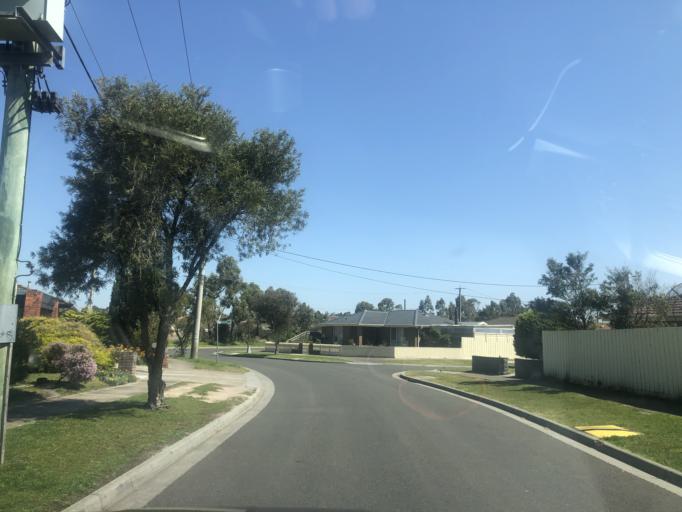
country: AU
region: Victoria
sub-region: Casey
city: Narre Warren South
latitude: -38.0459
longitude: 145.2799
